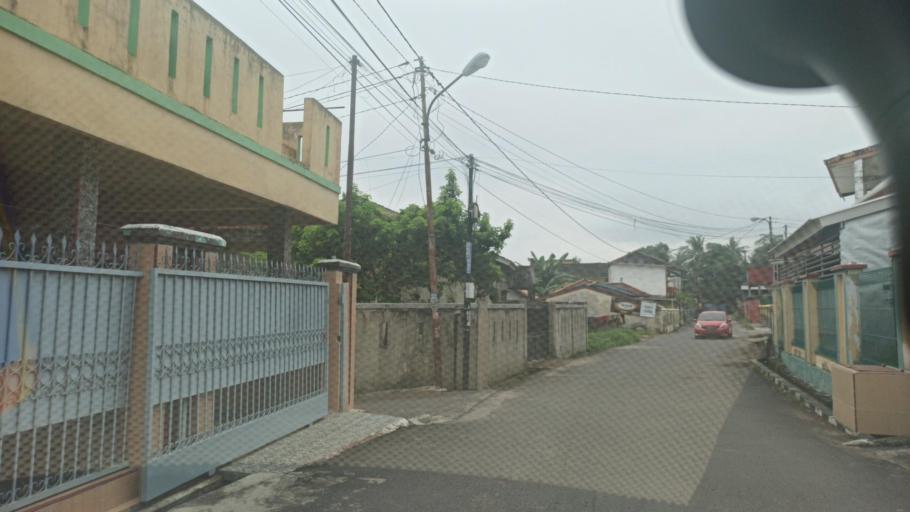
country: ID
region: South Sumatra
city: Palembang
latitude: -2.9315
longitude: 104.7752
